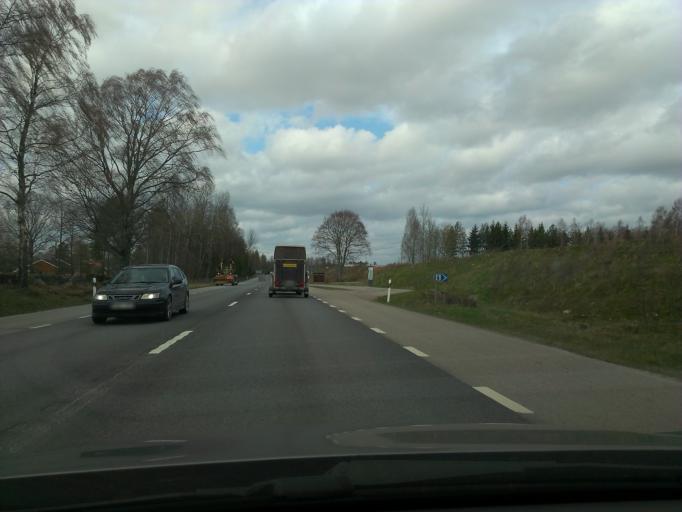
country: SE
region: Kronoberg
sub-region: Vaxjo Kommun
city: Vaexjoe
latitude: 56.8723
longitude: 14.7411
